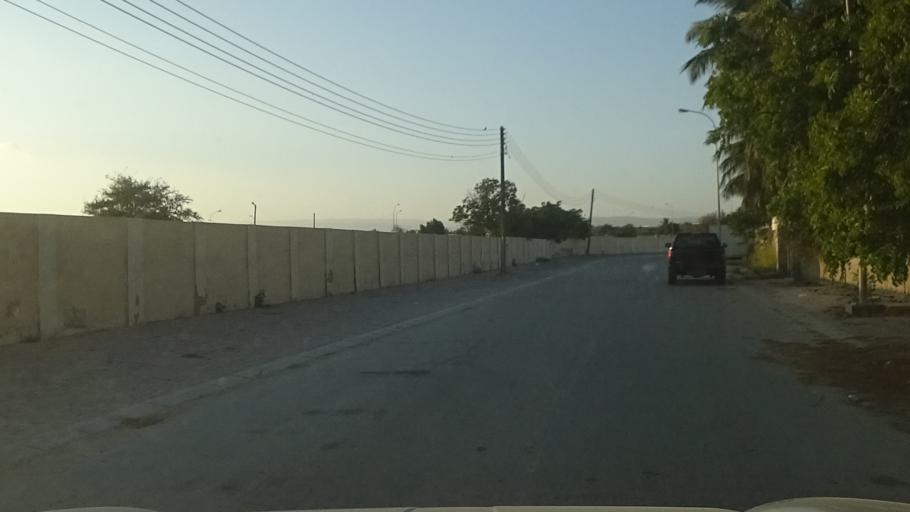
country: OM
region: Zufar
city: Salalah
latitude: 17.0270
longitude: 54.1707
